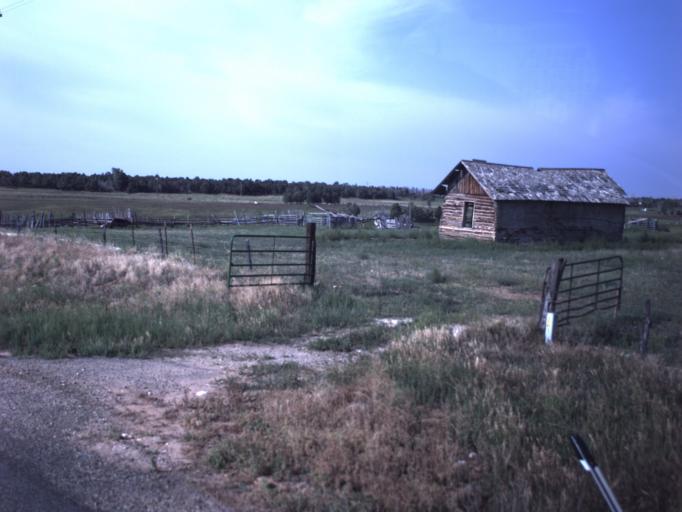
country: US
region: Utah
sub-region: Duchesne County
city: Duchesne
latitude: 40.3357
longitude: -110.4079
